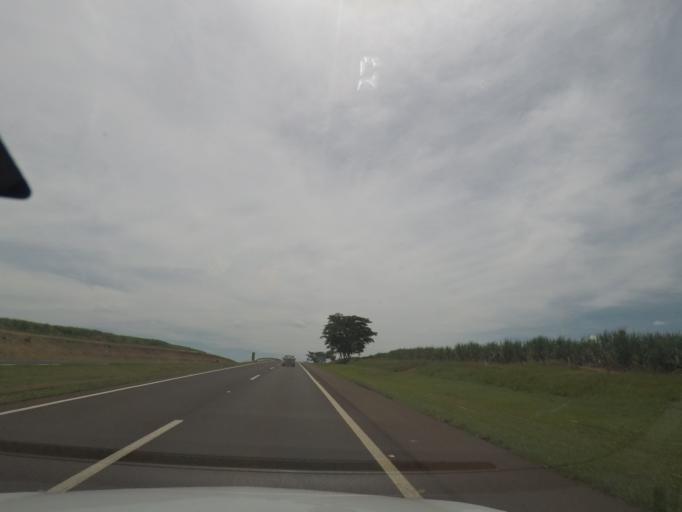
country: BR
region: Sao Paulo
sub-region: Bebedouro
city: Bebedouro
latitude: -21.0478
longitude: -48.4152
